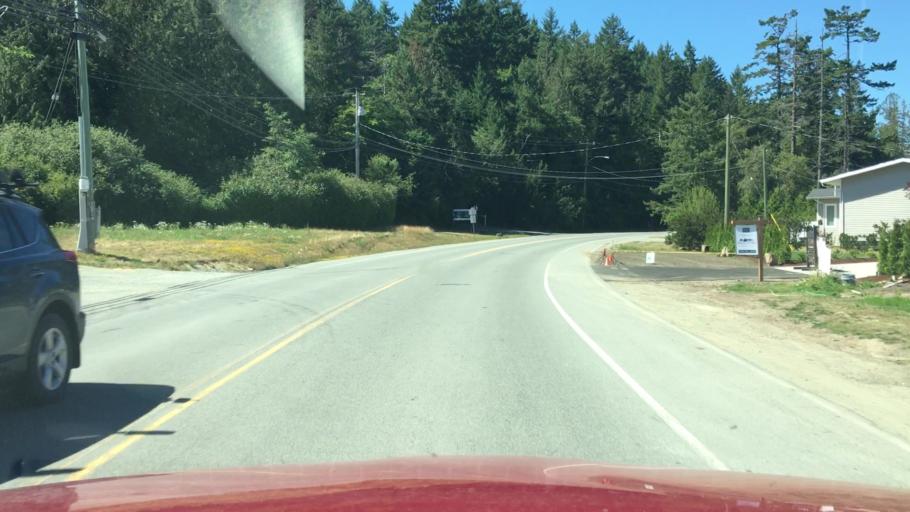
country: CA
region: British Columbia
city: North Saanich
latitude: 48.6723
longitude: -123.4234
